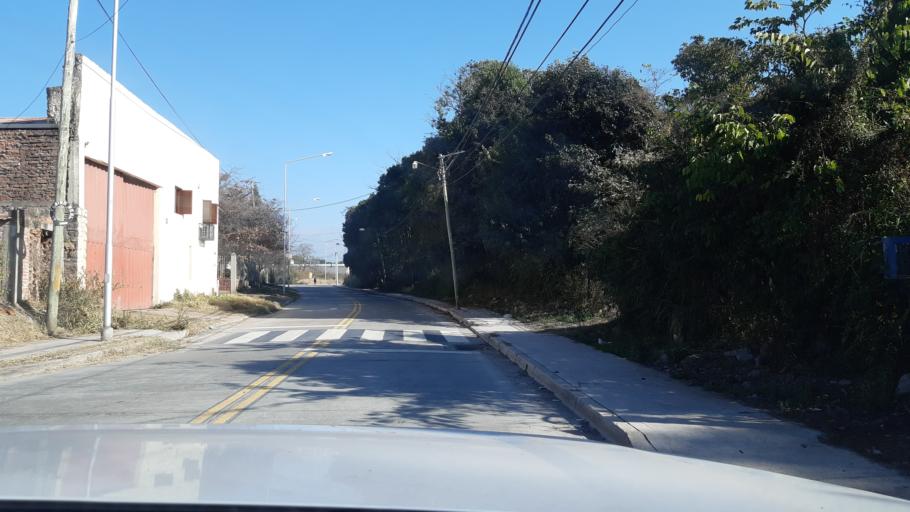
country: AR
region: Jujuy
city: Palpala
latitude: -24.2282
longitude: -65.2407
